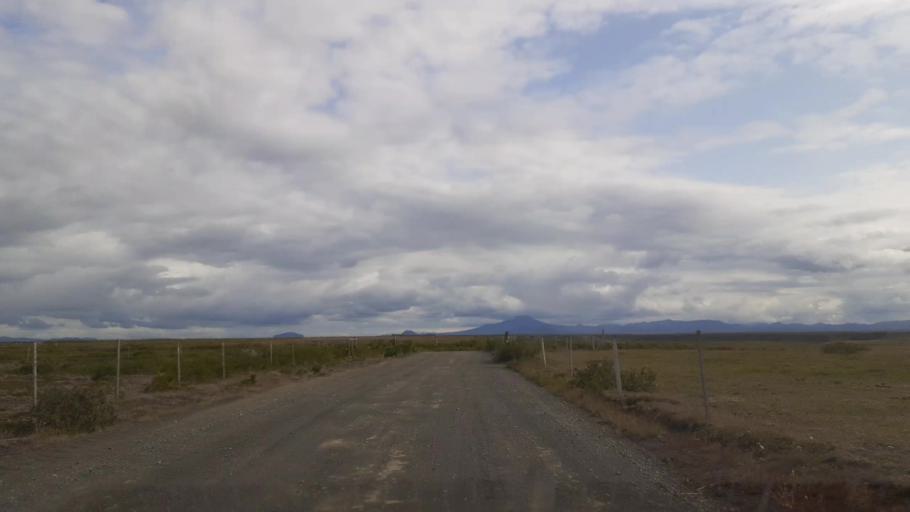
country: IS
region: South
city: Vestmannaeyjar
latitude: 63.8234
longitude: -20.3646
